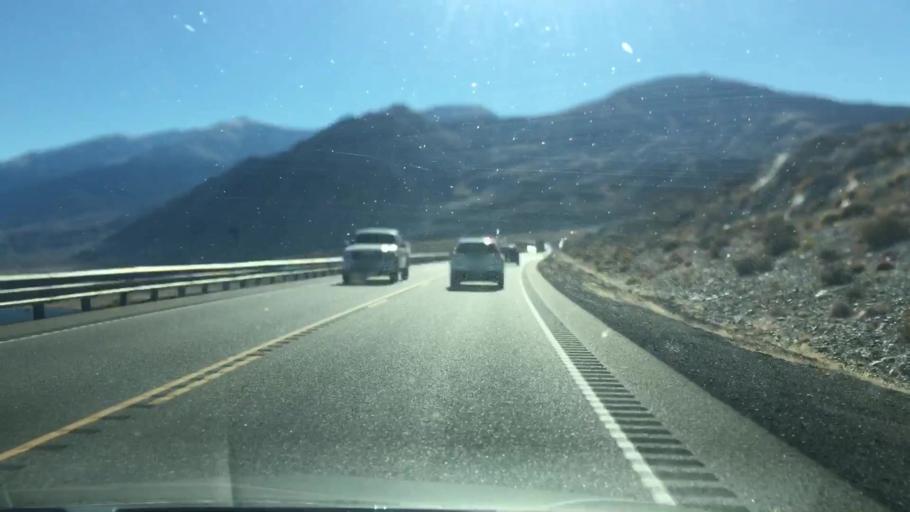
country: US
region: Nevada
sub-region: Mineral County
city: Hawthorne
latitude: 38.7061
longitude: -118.7652
